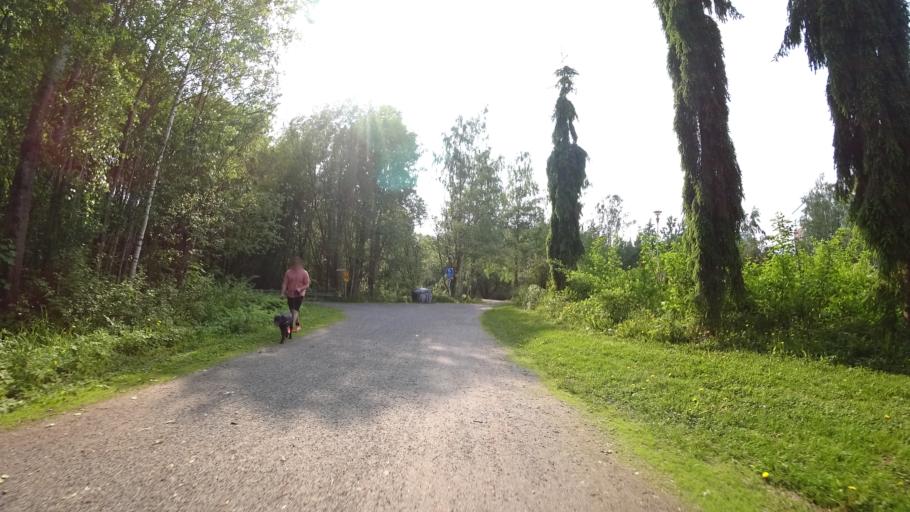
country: FI
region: Pirkanmaa
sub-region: Tampere
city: Pirkkala
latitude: 61.5054
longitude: 23.6804
